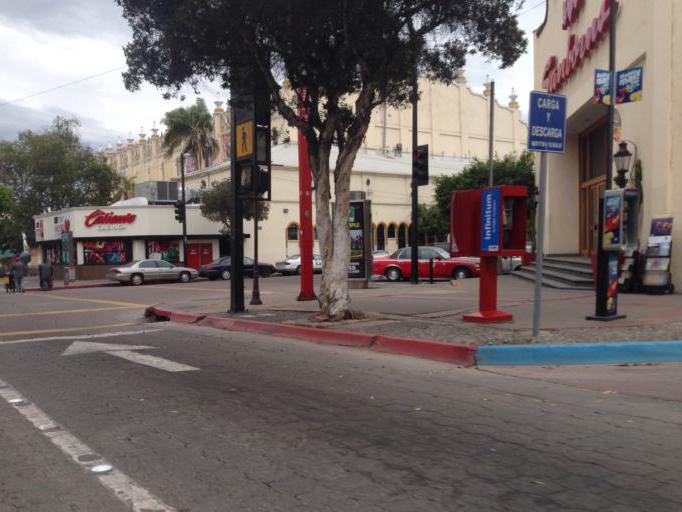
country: MX
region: Baja California
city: Tijuana
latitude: 32.5280
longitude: -117.0361
